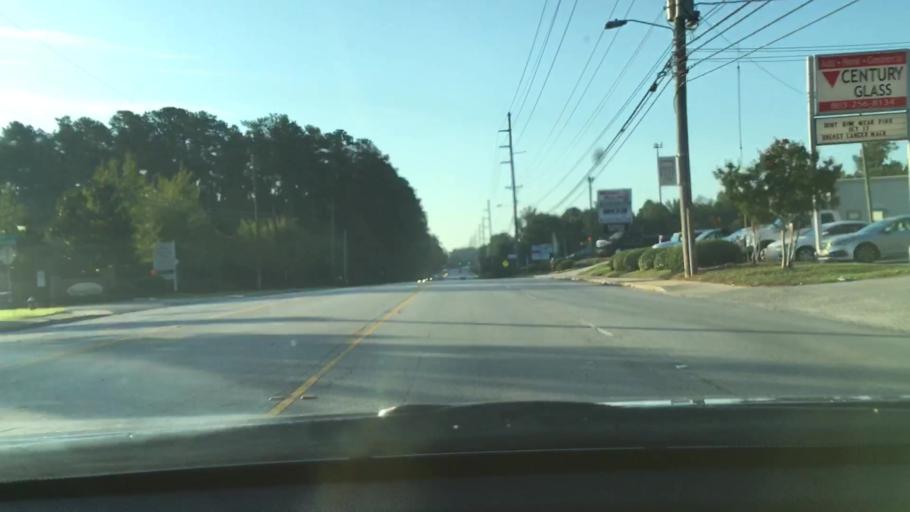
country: US
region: South Carolina
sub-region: Lexington County
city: Saint Andrews
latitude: 34.0632
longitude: -81.1150
